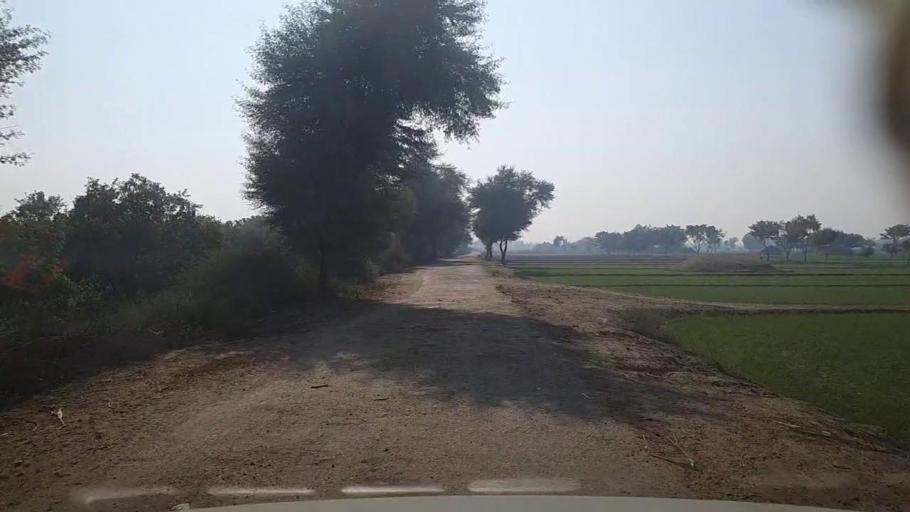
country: PK
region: Sindh
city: Kandiari
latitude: 26.9850
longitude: 68.4693
